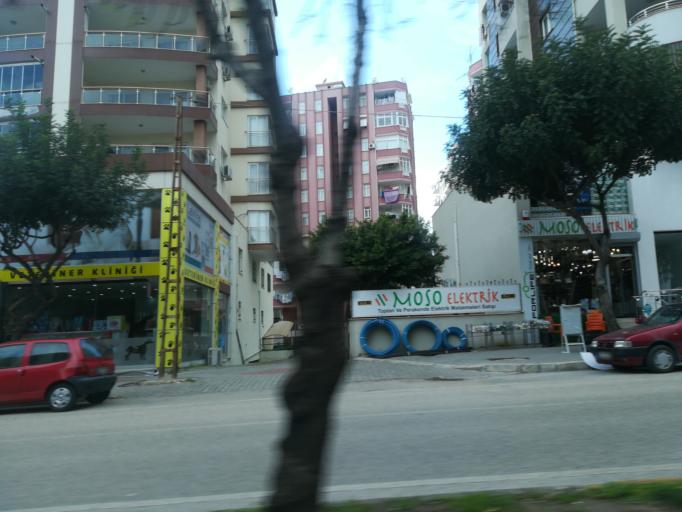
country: TR
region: Adana
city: Adana
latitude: 37.0373
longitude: 35.2993
